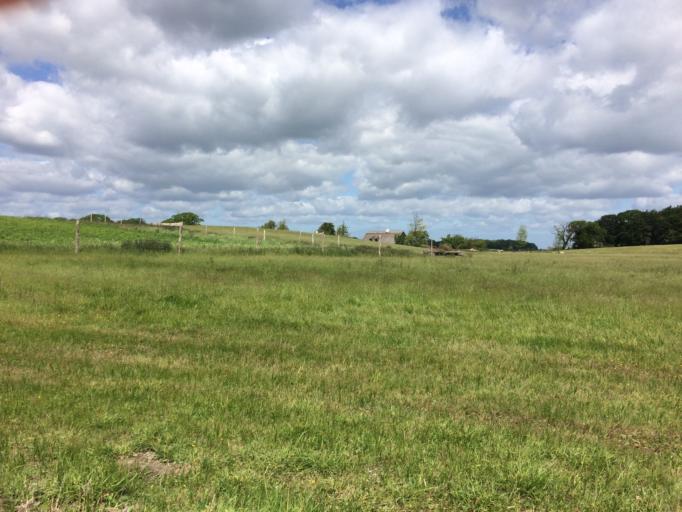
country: DK
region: Zealand
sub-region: Roskilde Kommune
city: Svogerslev
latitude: 55.6887
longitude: 12.0075
